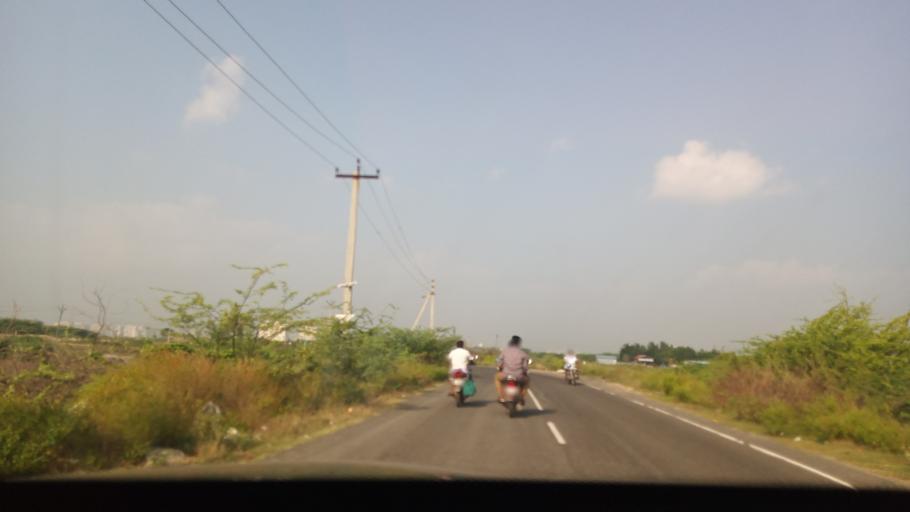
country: IN
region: Tamil Nadu
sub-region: Kancheepuram
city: Injambakkam
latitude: 12.7841
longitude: 80.2422
